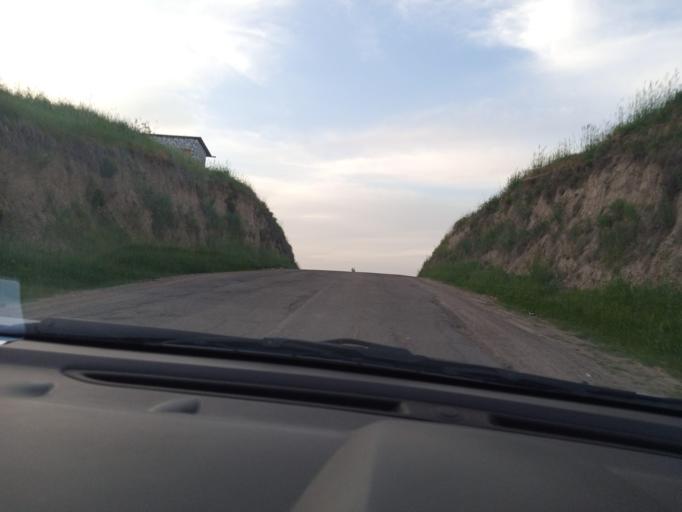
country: UZ
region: Toshkent
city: Parkent
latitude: 41.2347
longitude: 69.7374
